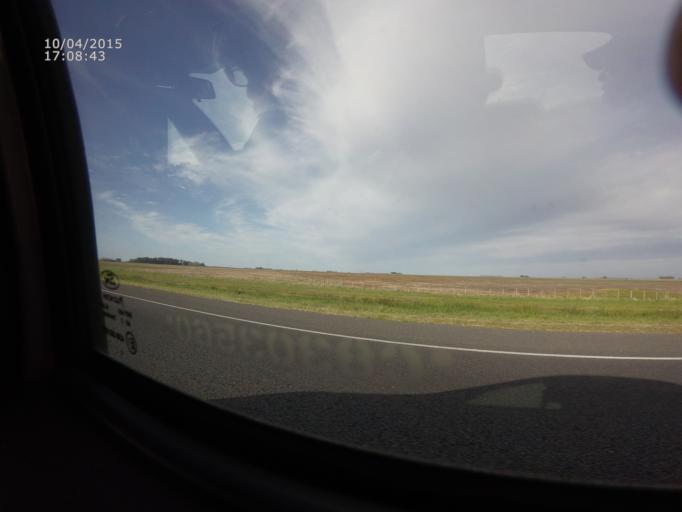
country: AR
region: Buenos Aires
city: Coronel Vidal
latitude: -37.3265
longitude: -57.7636
